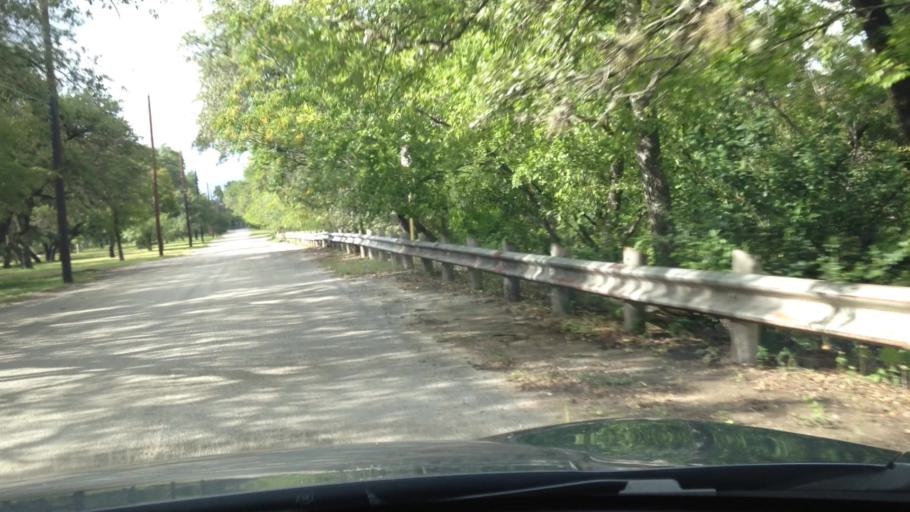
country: US
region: Texas
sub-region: Bexar County
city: Cross Mountain
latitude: 29.6282
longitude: -98.6089
